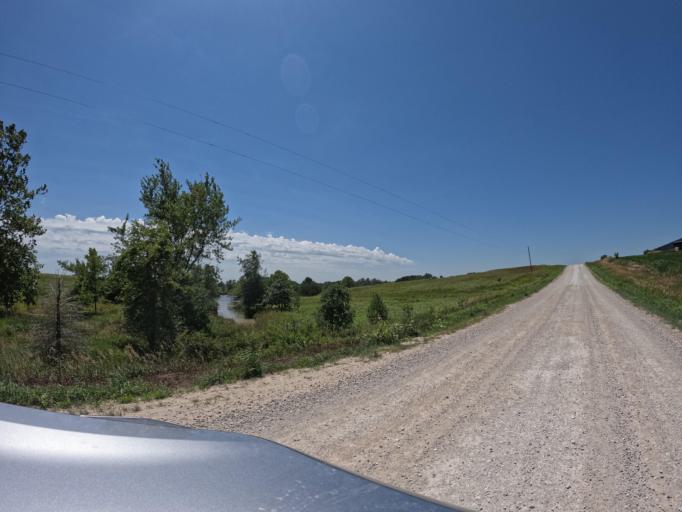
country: US
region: Iowa
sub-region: Keokuk County
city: Sigourney
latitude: 41.4089
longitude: -92.3273
